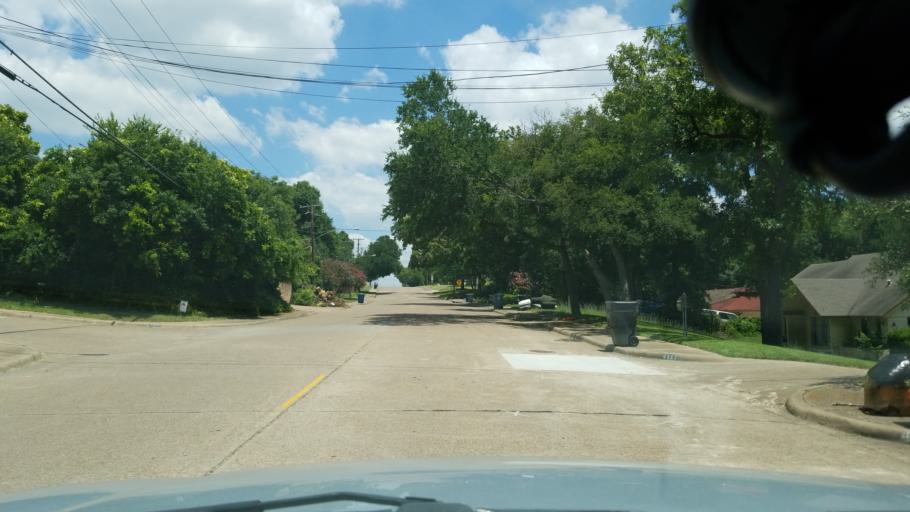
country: US
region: Texas
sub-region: Dallas County
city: Cockrell Hill
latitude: 32.6931
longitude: -96.8743
